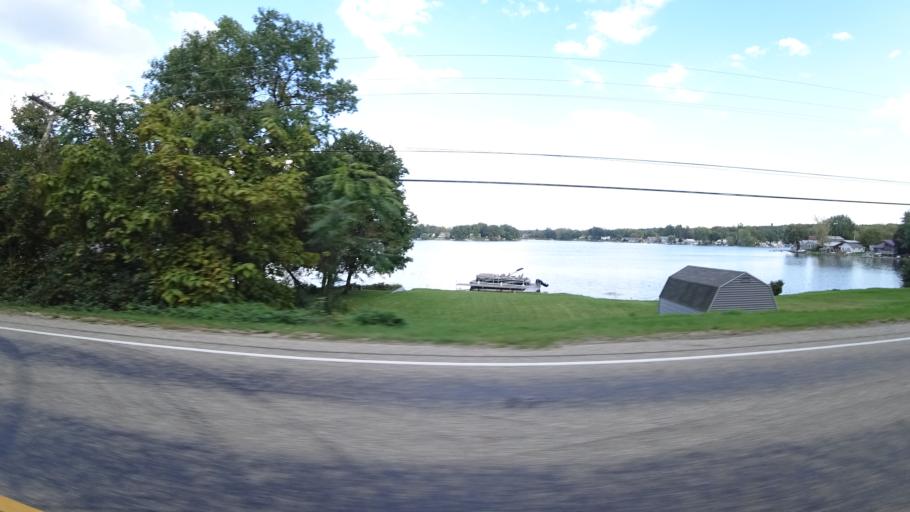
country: US
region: Michigan
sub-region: Saint Joseph County
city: Sturgis
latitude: 41.8384
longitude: -85.4287
